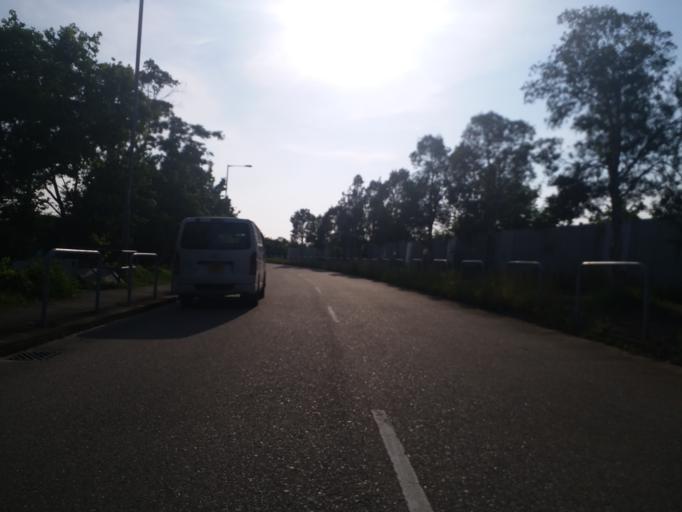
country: HK
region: Yuen Long
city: Yuen Long Kau Hui
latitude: 22.4793
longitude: 114.0559
